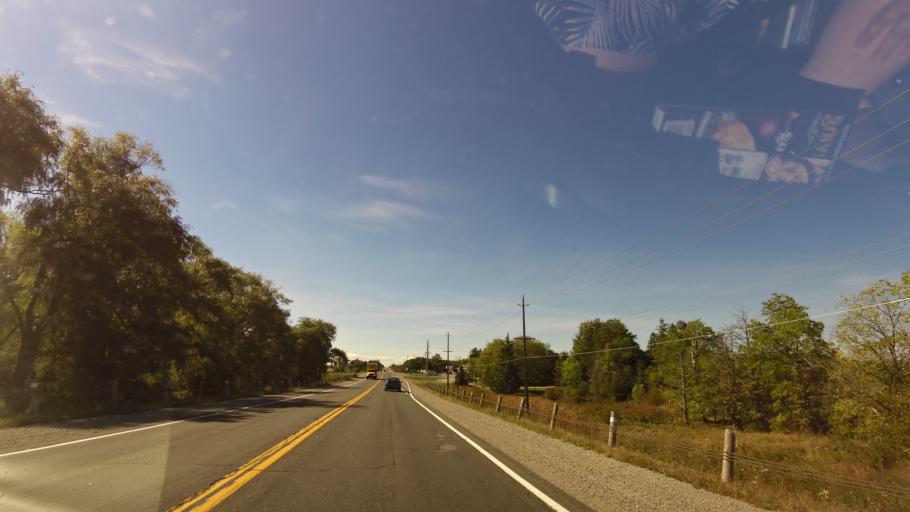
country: CA
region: Ontario
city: Ancaster
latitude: 43.0254
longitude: -79.9947
